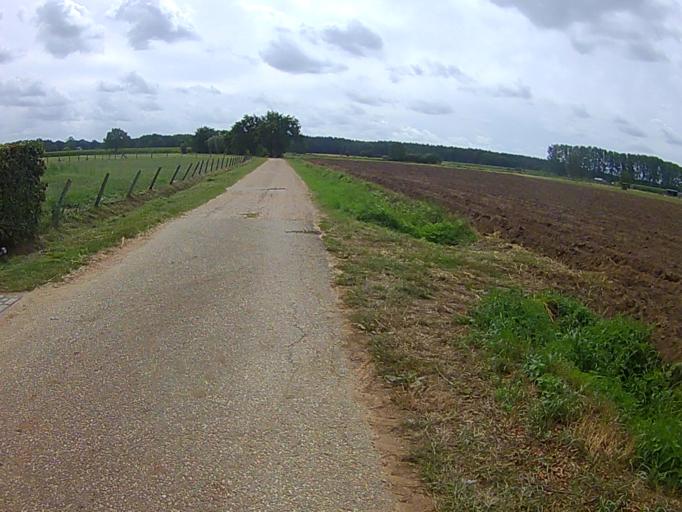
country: BE
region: Flanders
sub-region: Provincie Antwerpen
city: Lille
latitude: 51.2084
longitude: 4.8126
